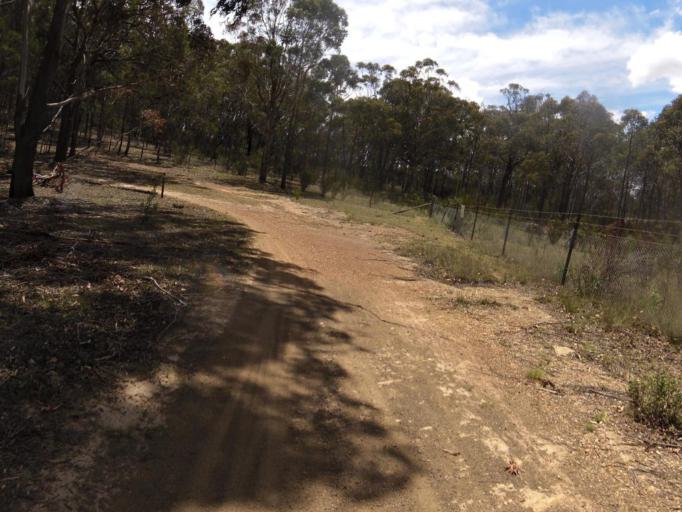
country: AU
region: Australian Capital Territory
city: Kaleen
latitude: -35.1266
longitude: 149.1284
